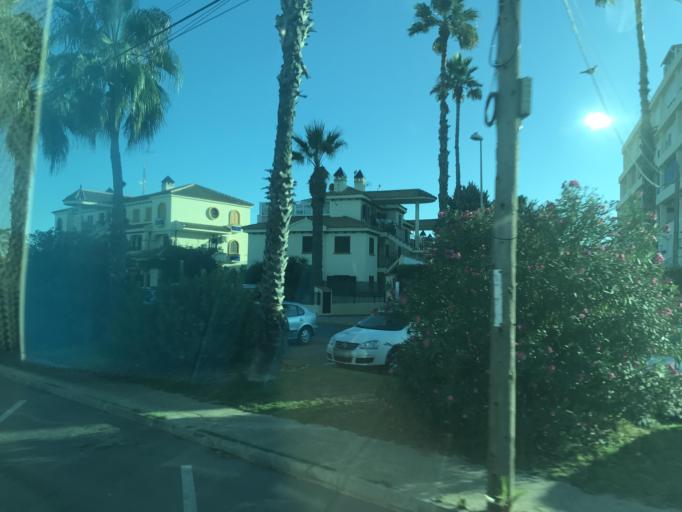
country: ES
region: Valencia
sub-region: Provincia de Alicante
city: Torrevieja
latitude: 38.0034
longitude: -0.6547
